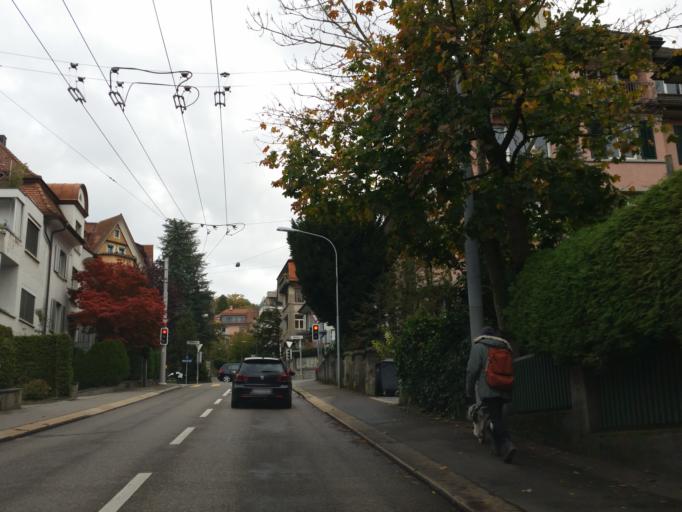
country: CH
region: Zurich
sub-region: Bezirk Zuerich
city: Zuerich (Kreis 7) / Hirslanden
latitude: 47.3625
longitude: 8.5674
